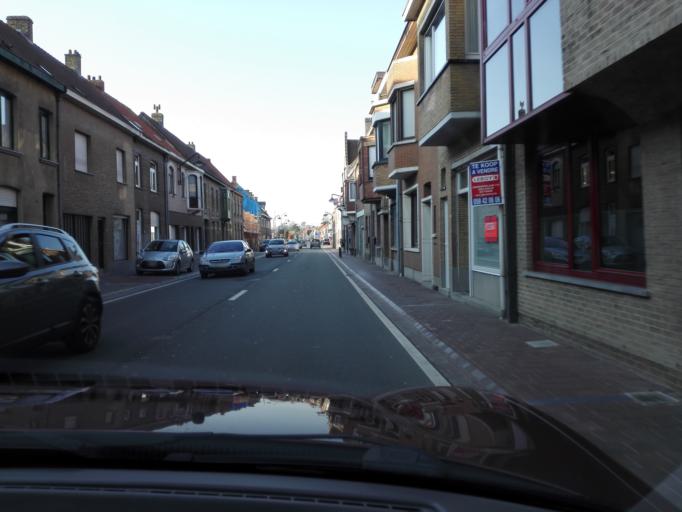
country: BE
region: Flanders
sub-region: Provincie West-Vlaanderen
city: De Panne
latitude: 51.0761
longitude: 2.6033
